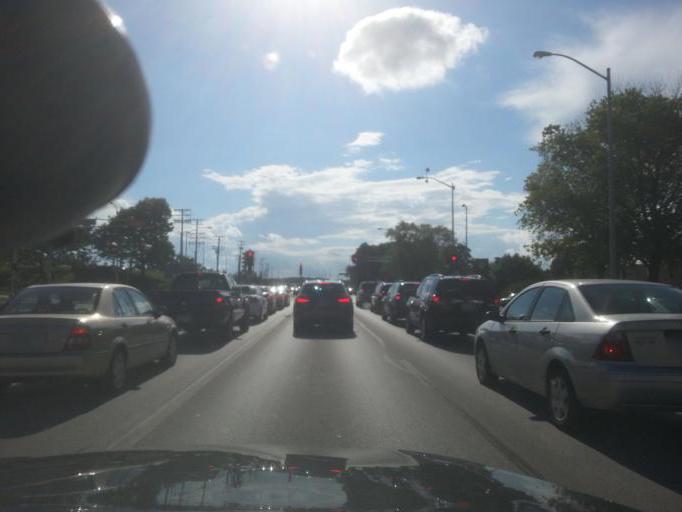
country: US
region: Wisconsin
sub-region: Dane County
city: Shorewood Hills
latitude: 43.0755
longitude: -89.4560
